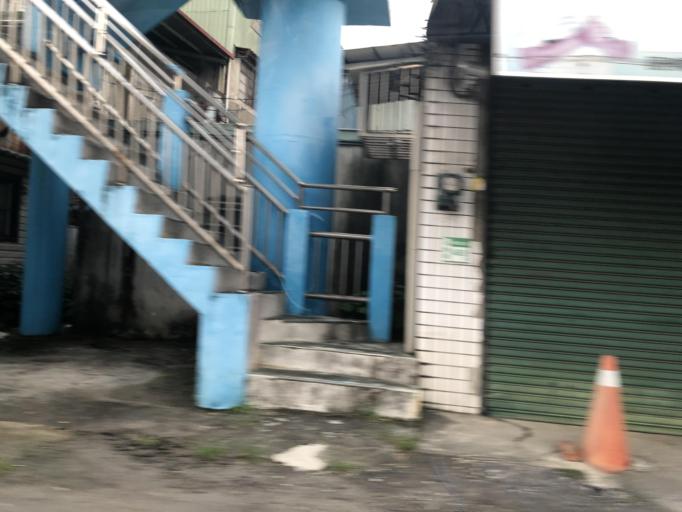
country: TW
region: Taiwan
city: Daxi
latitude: 24.9073
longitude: 121.3640
